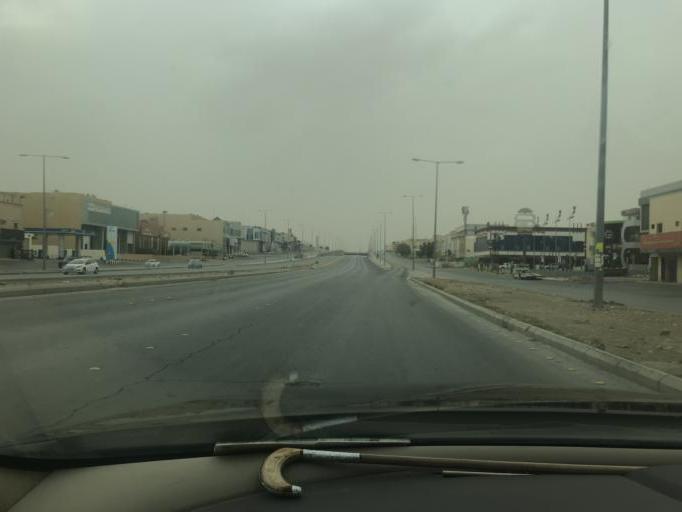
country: SA
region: Ar Riyad
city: Riyadh
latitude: 24.7736
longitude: 46.7103
